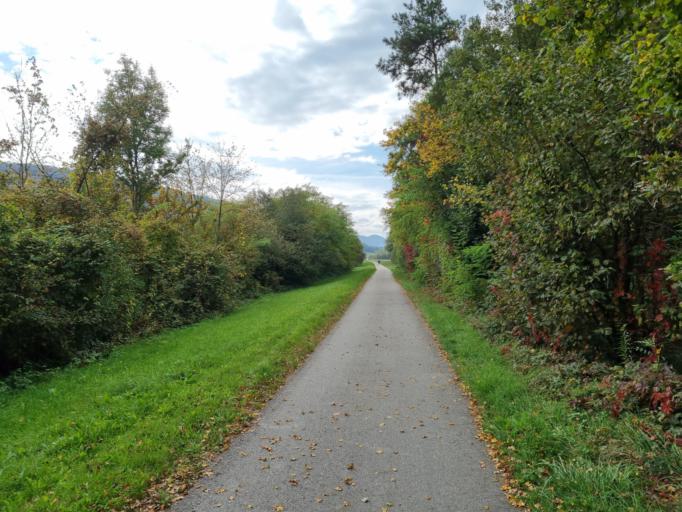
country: AT
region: Lower Austria
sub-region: Politischer Bezirk Sankt Polten
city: Wilhelmsburg
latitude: 48.1188
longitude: 15.6232
